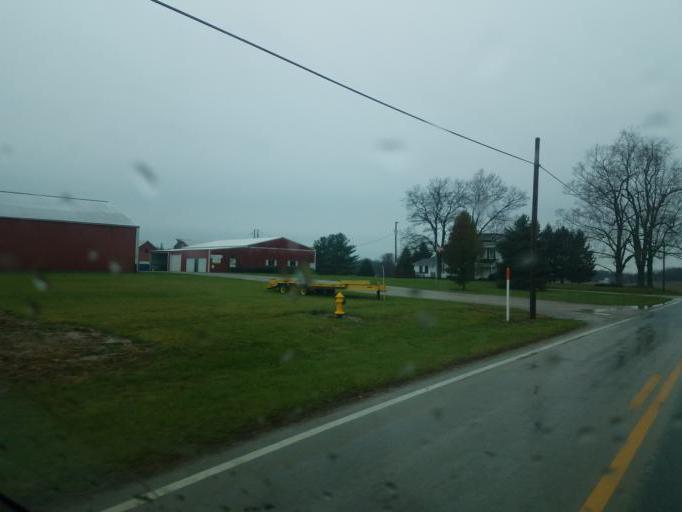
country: US
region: Ohio
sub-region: Knox County
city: Centerburg
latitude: 40.3215
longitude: -82.7620
